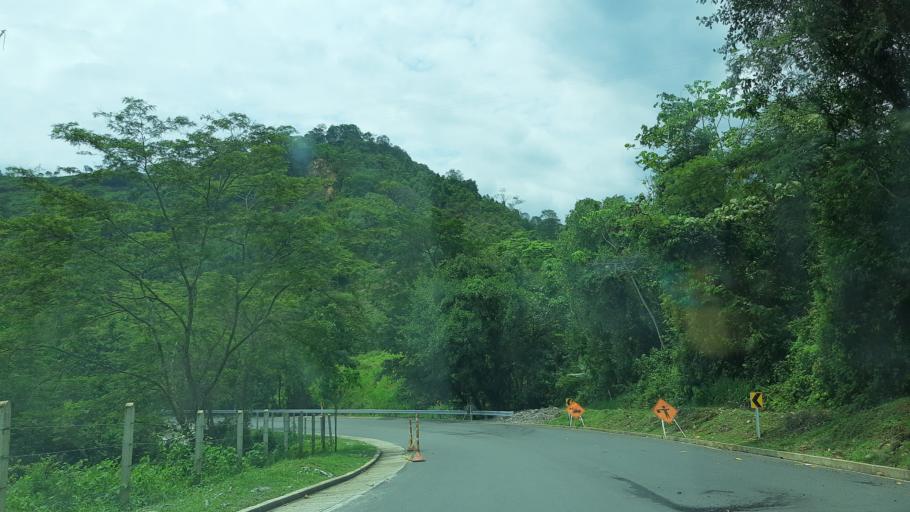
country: CO
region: Boyaca
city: San Luis de Gaceno
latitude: 4.8335
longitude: -73.1220
